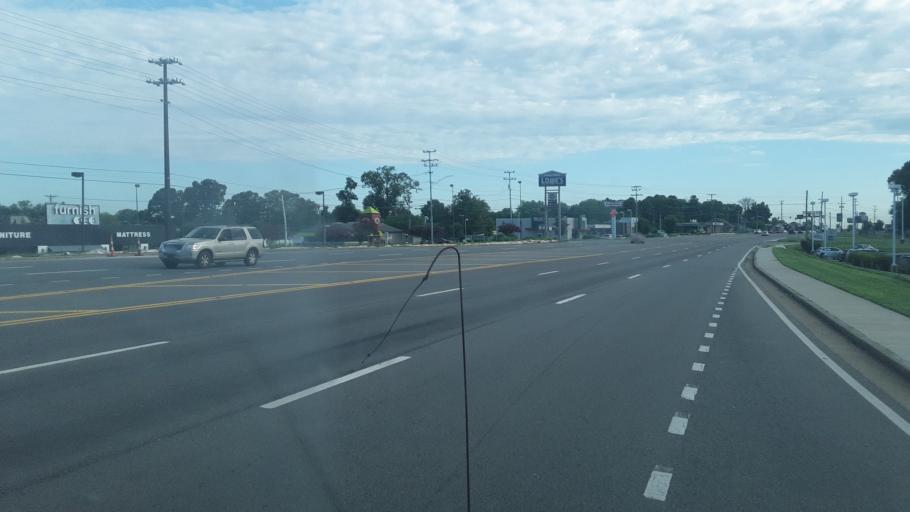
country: US
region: Tennessee
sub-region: Montgomery County
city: Clarksville
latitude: 36.5735
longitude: -87.3029
